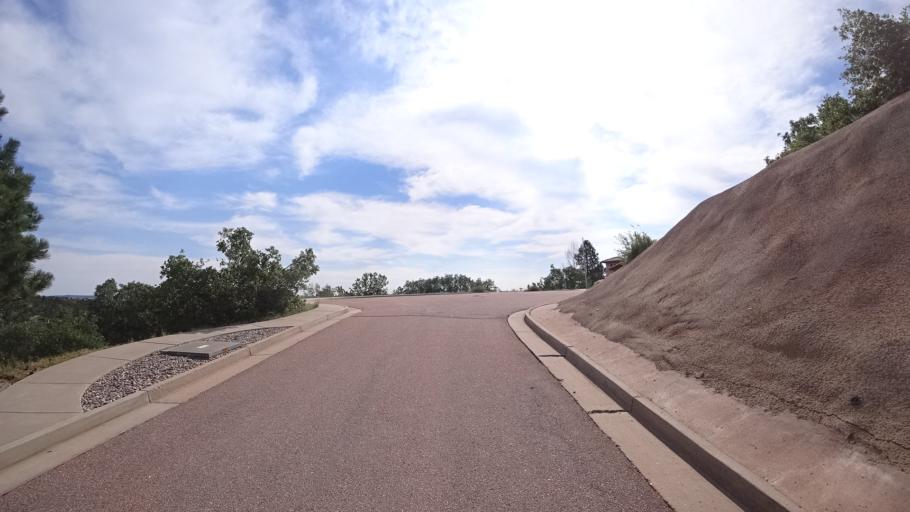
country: US
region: Colorado
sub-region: El Paso County
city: Air Force Academy
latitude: 38.9413
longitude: -104.8604
